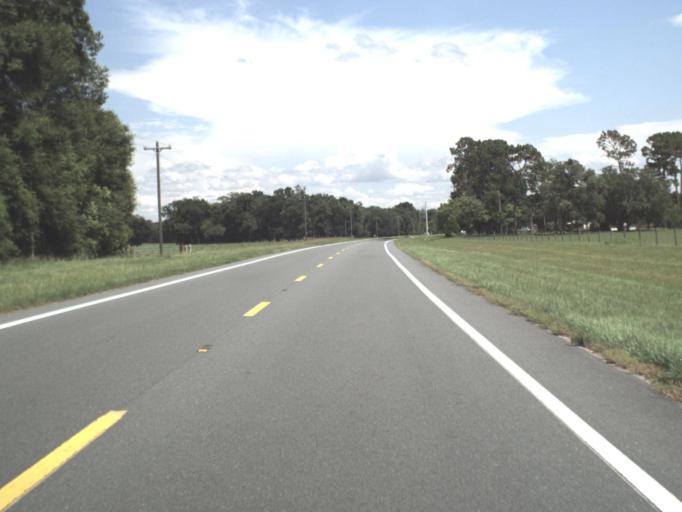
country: US
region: Florida
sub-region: Lafayette County
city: Mayo
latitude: 30.1251
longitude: -83.2713
